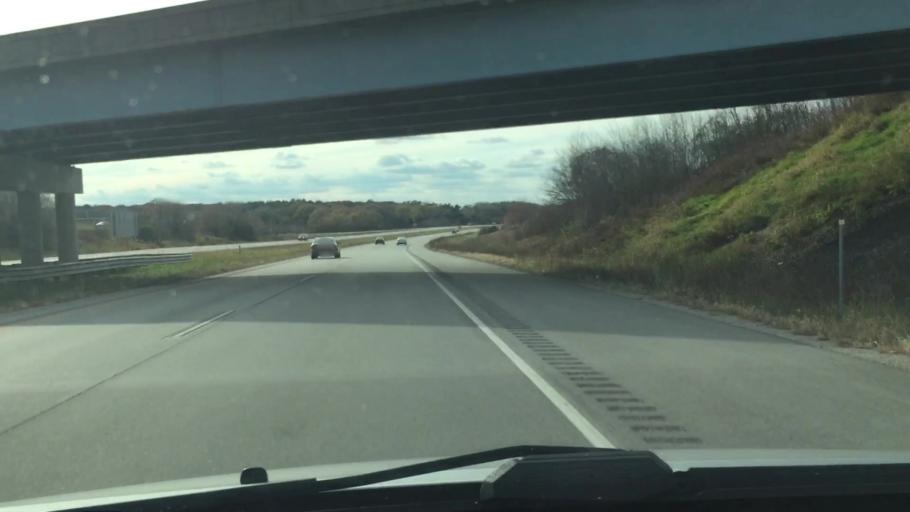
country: US
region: Wisconsin
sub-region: Waukesha County
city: Hartland
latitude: 43.1053
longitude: -88.3625
